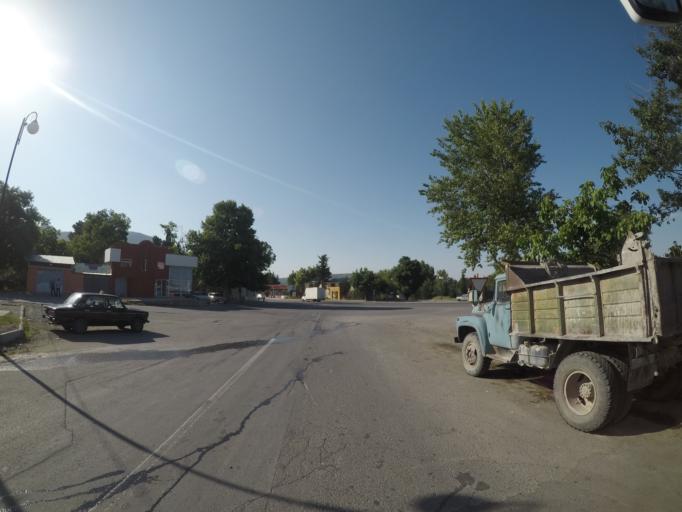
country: AZ
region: Shaki City
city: Sheki
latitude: 41.2072
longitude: 47.1675
